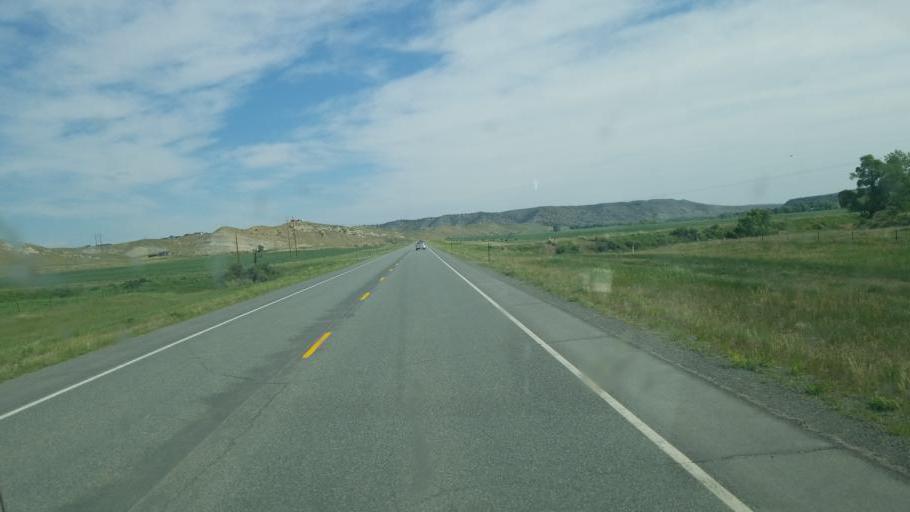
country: US
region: Wyoming
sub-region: Park County
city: Cody
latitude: 44.1671
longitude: -108.8763
